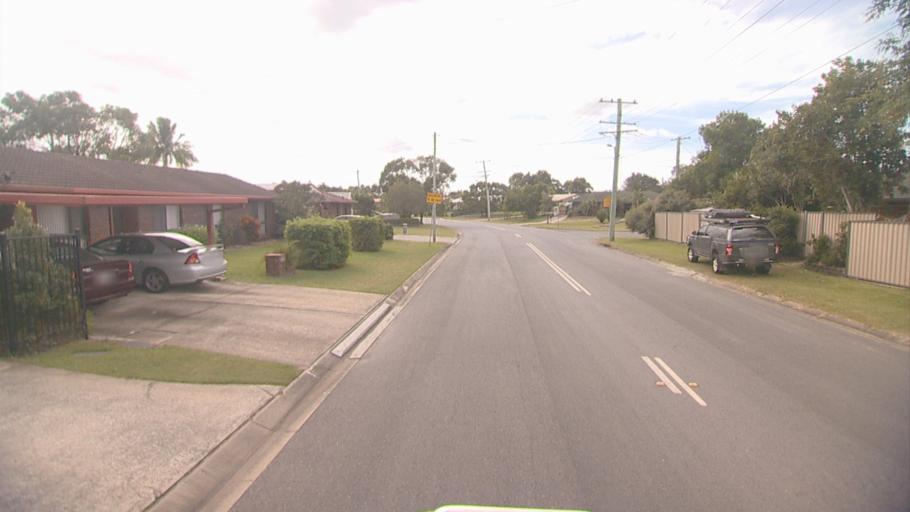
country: AU
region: Queensland
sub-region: Logan
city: Waterford West
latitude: -27.6829
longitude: 153.1526
